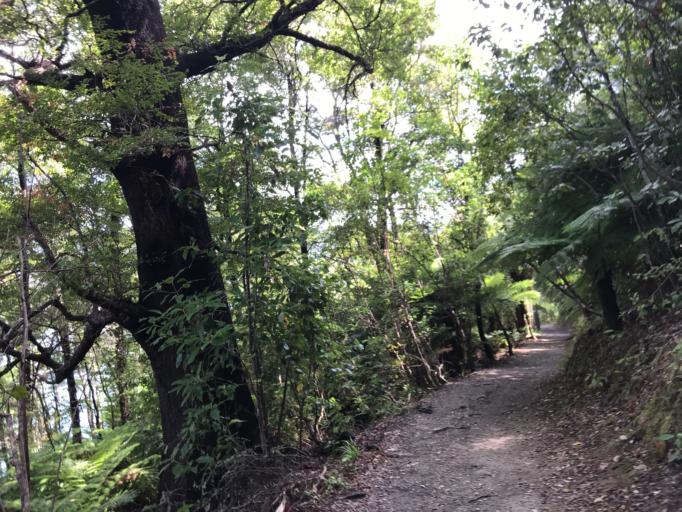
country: NZ
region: Marlborough
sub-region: Marlborough District
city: Picton
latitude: -41.2640
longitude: 173.9246
